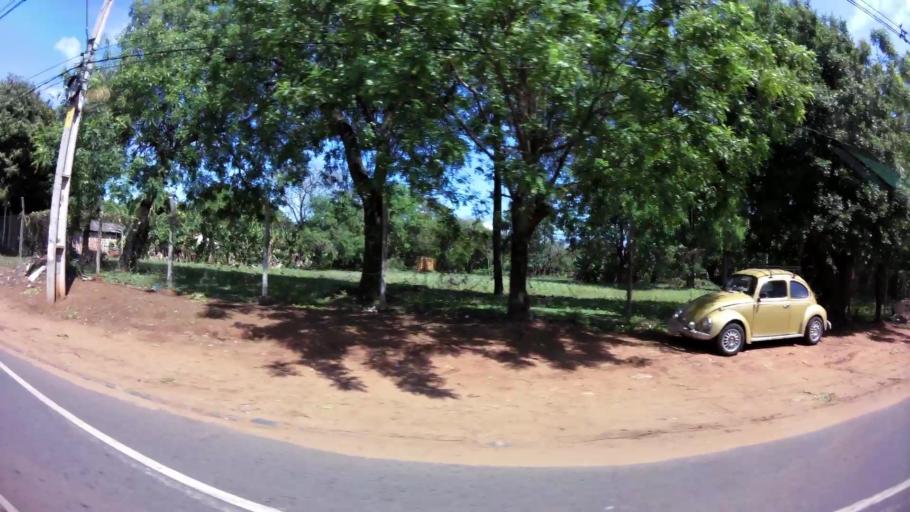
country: PY
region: Central
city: San Lorenzo
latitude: -25.3141
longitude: -57.5069
